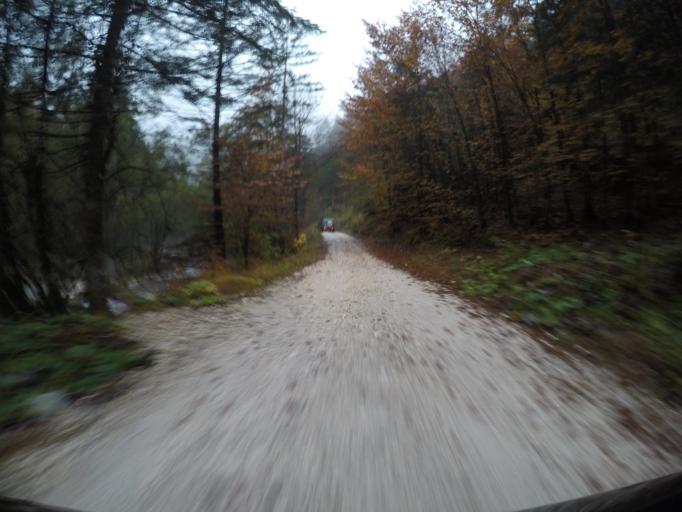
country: SI
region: Kranjska Gora
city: Kranjska Gora
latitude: 46.3830
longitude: 13.7695
